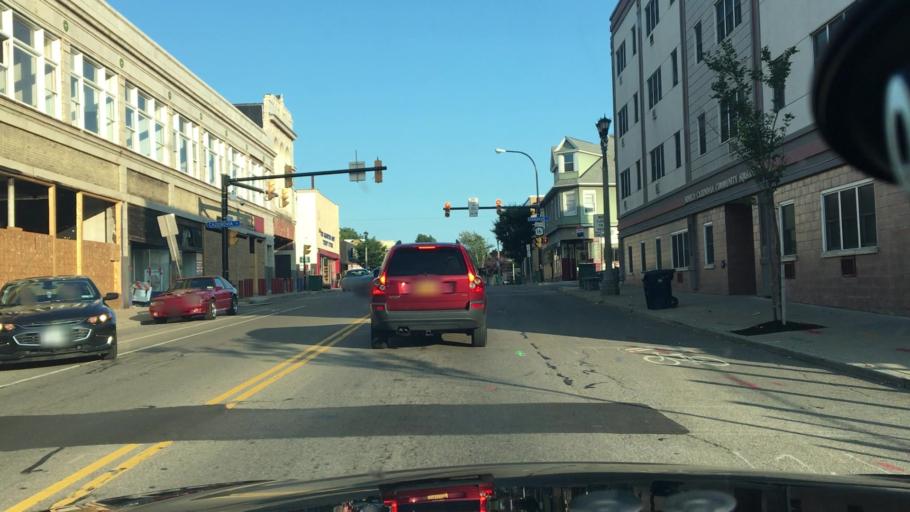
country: US
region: New York
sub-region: Erie County
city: West Seneca
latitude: 42.8535
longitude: -78.8077
